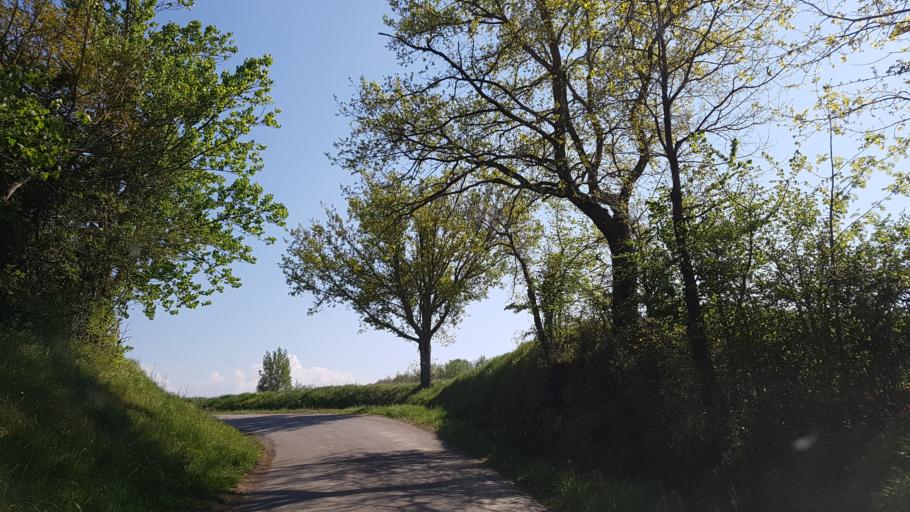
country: FR
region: Midi-Pyrenees
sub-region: Departement de l'Ariege
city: La Tour-du-Crieu
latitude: 43.0959
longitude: 1.7181
